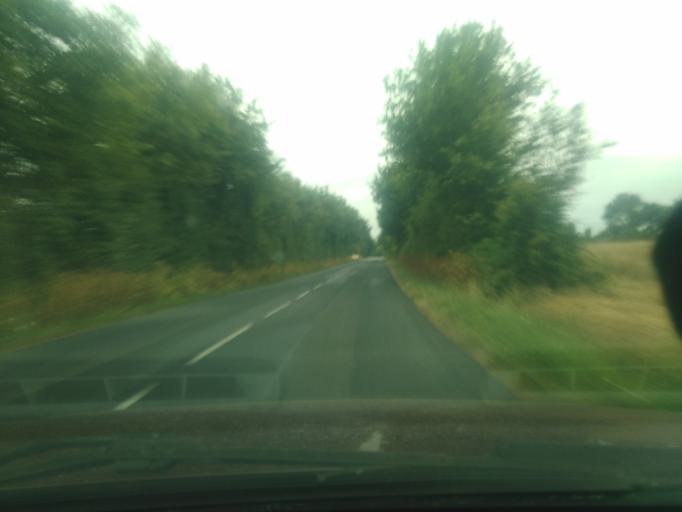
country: FR
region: Pays de la Loire
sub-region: Departement de la Vendee
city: Saint-Denis-la-Chevasse
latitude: 46.7886
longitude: -1.3131
